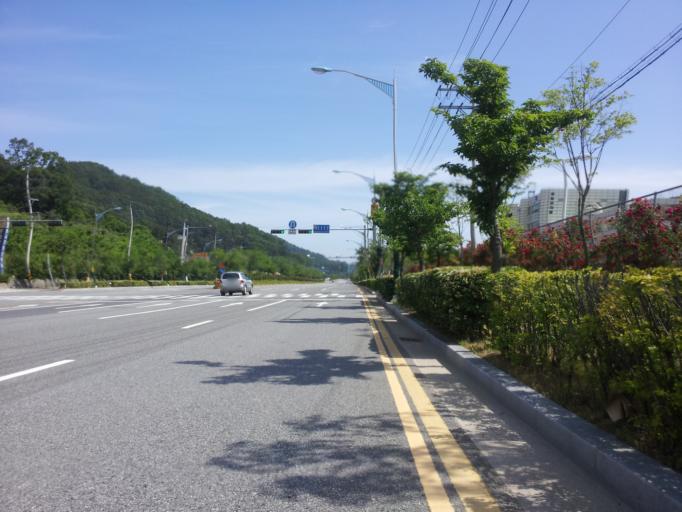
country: KR
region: Daejeon
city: Daejeon
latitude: 36.3221
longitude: 127.4722
